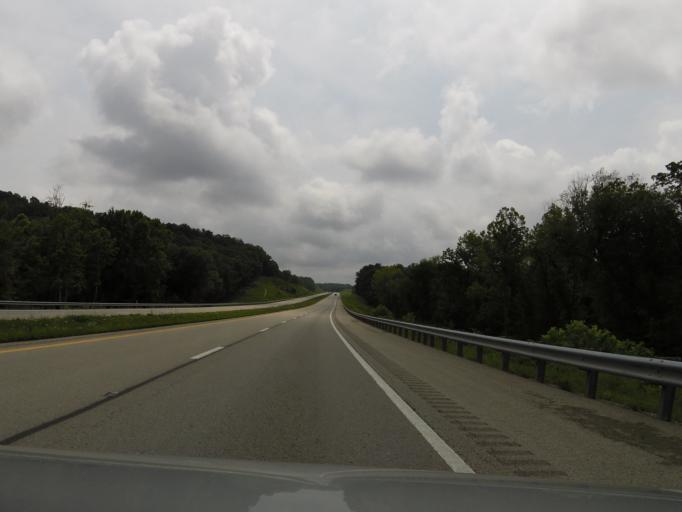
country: US
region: Kentucky
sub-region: Ohio County
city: Oak Grove
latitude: 37.3879
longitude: -86.6720
